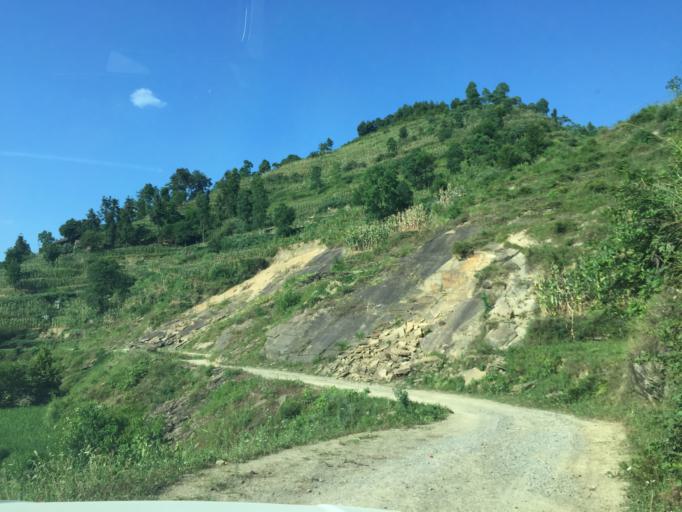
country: CN
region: Guizhou Sheng
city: Tongjing
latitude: 28.3336
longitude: 108.2950
